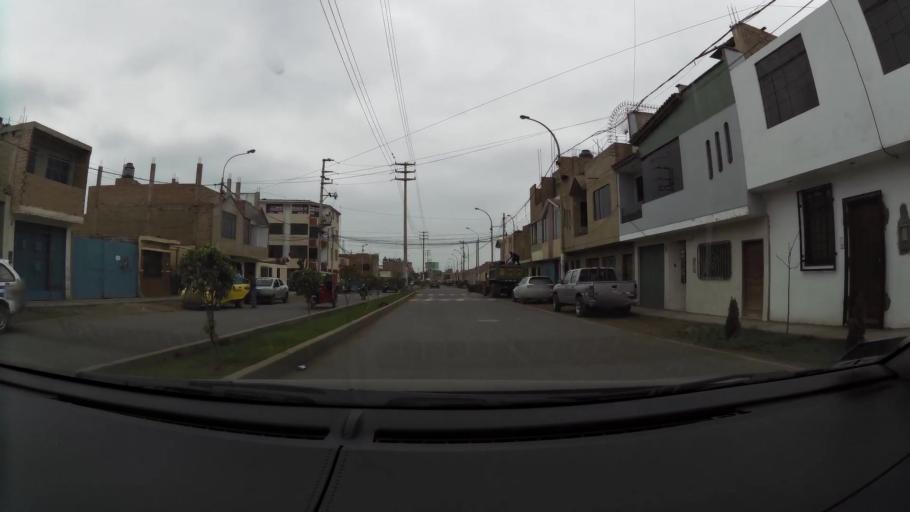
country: PE
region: Lima
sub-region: Provincia de Huaral
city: Huaral
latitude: -11.5002
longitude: -77.2036
